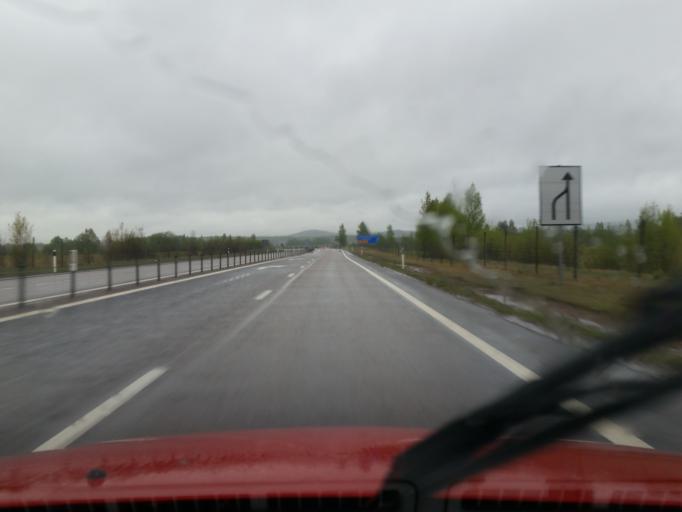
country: SE
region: Dalarna
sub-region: Borlange Kommun
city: Ornas
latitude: 60.4272
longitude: 15.5305
